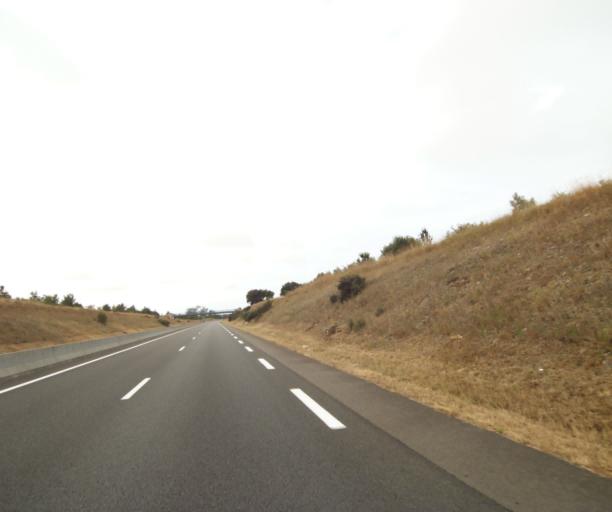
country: FR
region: Pays de la Loire
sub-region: Departement de la Vendee
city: Chateau-d'Olonne
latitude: 46.5047
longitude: -1.7027
